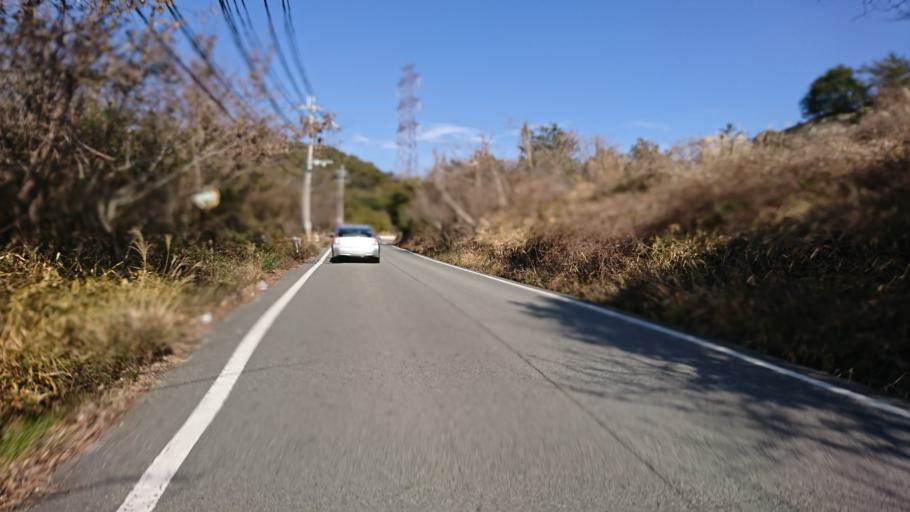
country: JP
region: Hyogo
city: Kakogawacho-honmachi
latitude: 34.7966
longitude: 134.8396
